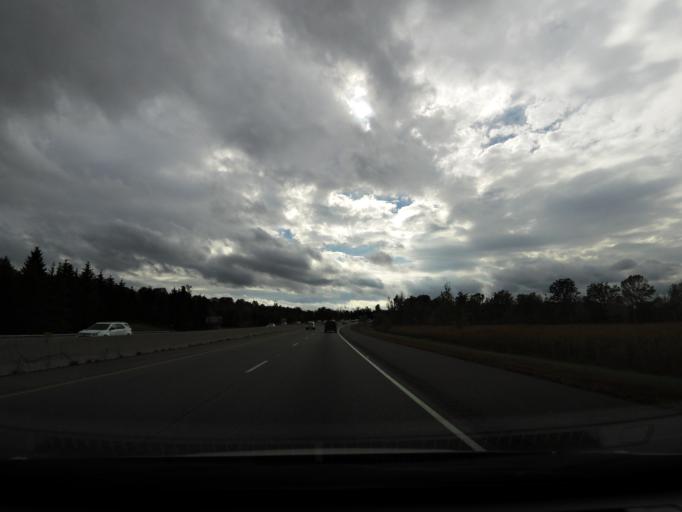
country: CA
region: Ontario
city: Kingston
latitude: 44.2979
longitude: -76.4153
